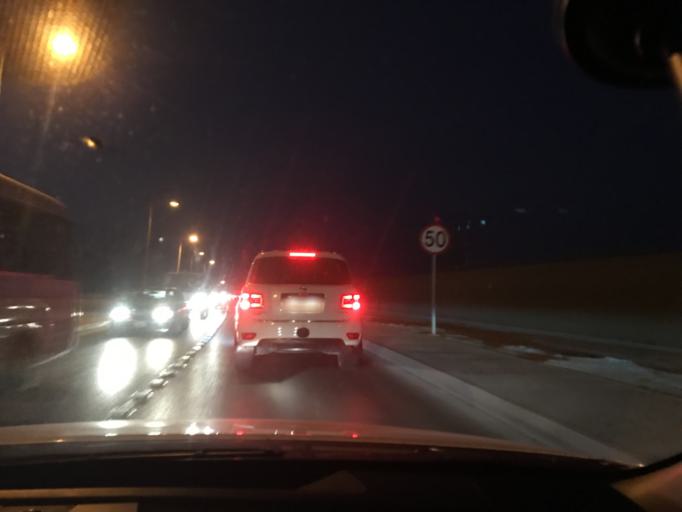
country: BH
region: Muharraq
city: Al Muharraq
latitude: 26.2800
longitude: 50.6133
